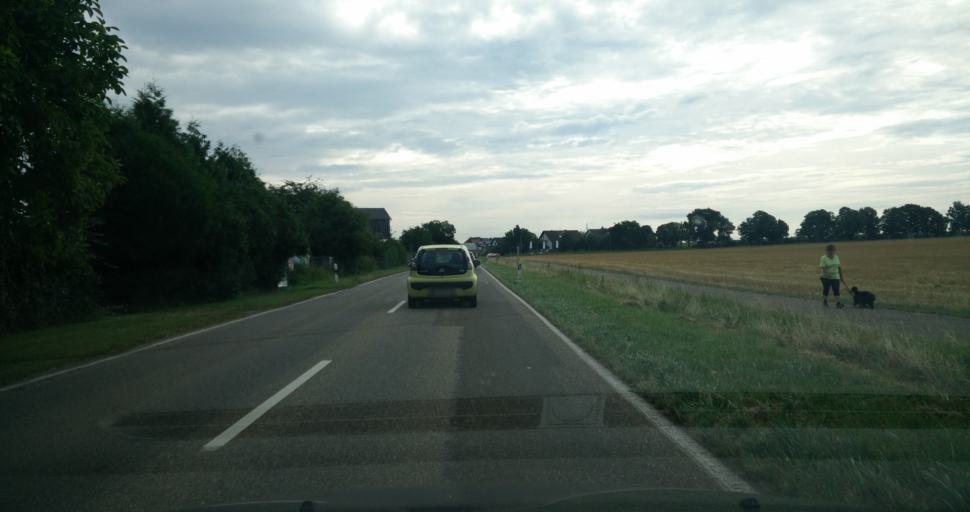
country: DE
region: Rheinland-Pfalz
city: Kandel
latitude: 49.0944
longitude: 8.1835
